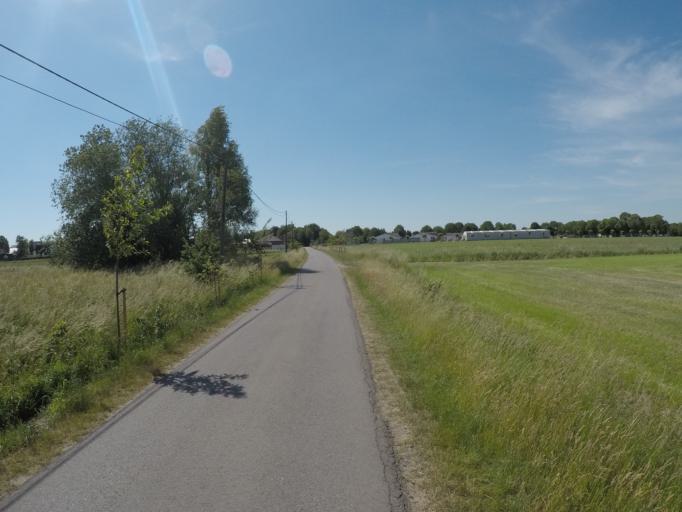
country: BE
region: Flanders
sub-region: Provincie Antwerpen
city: Wuustwezel
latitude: 51.4058
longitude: 4.6396
